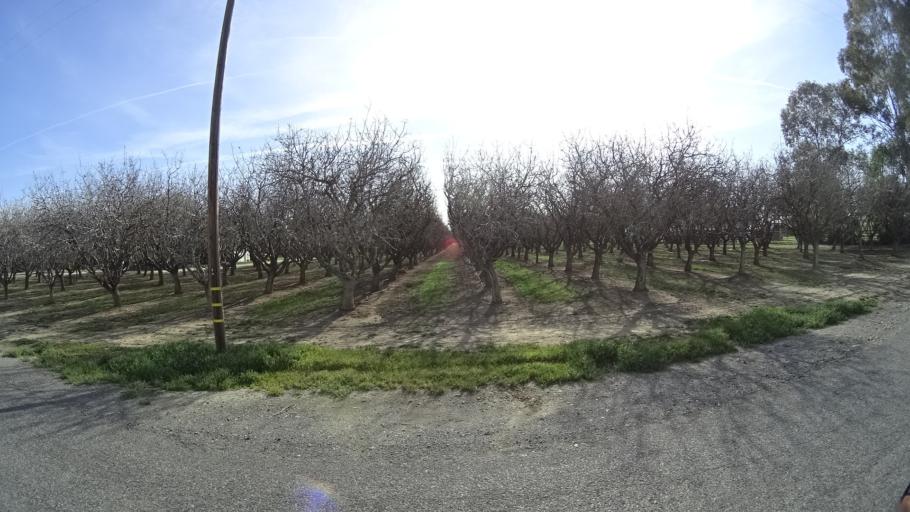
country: US
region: California
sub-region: Glenn County
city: Orland
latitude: 39.7066
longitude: -122.2158
